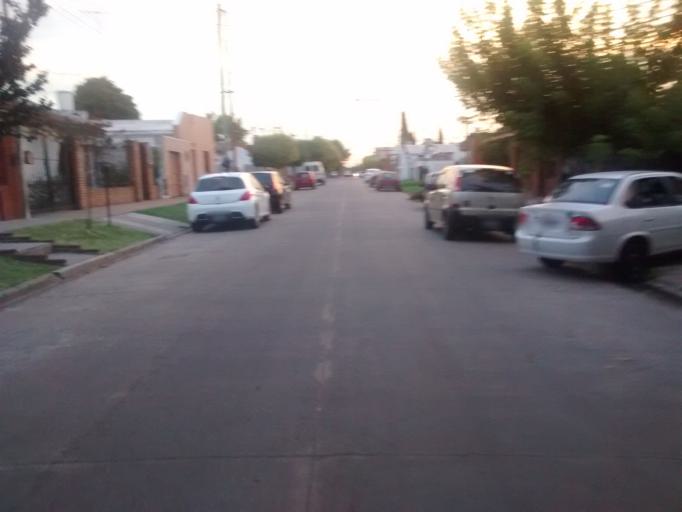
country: AR
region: Buenos Aires
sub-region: Partido de La Plata
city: La Plata
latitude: -34.9408
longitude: -57.9314
